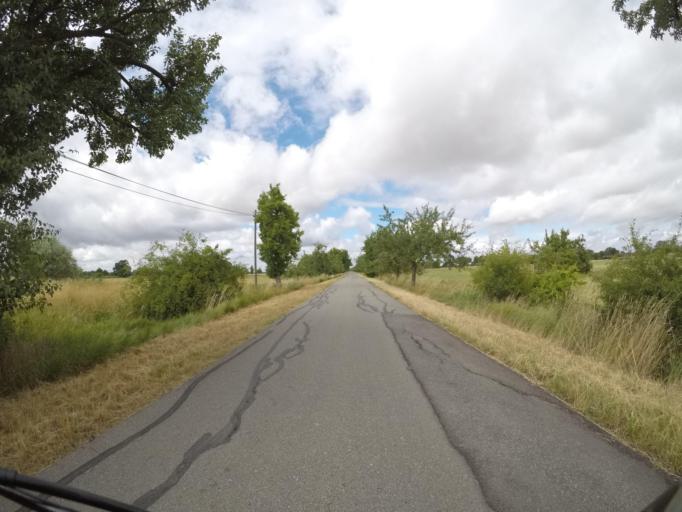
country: DE
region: Lower Saxony
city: Dannenberg
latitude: 53.1484
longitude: 11.1025
